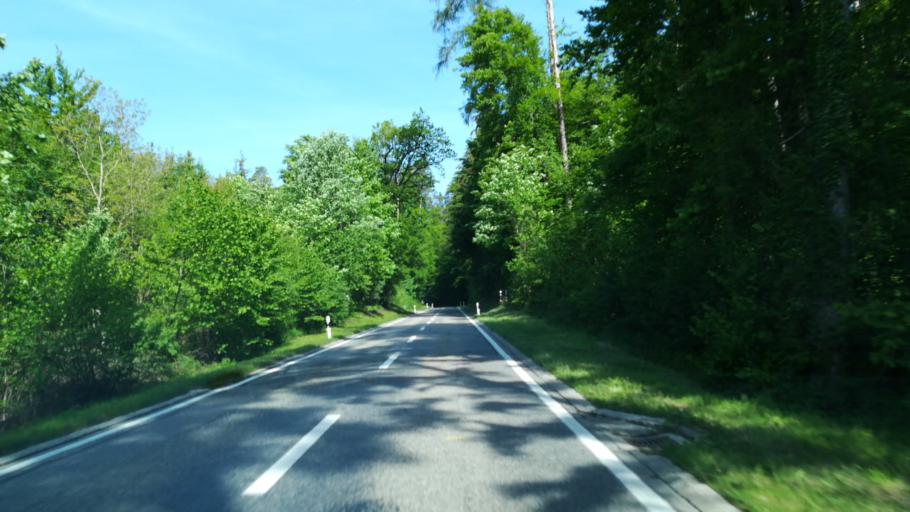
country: CH
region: Thurgau
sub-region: Frauenfeld District
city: Pfyn
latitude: 47.6069
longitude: 8.9388
